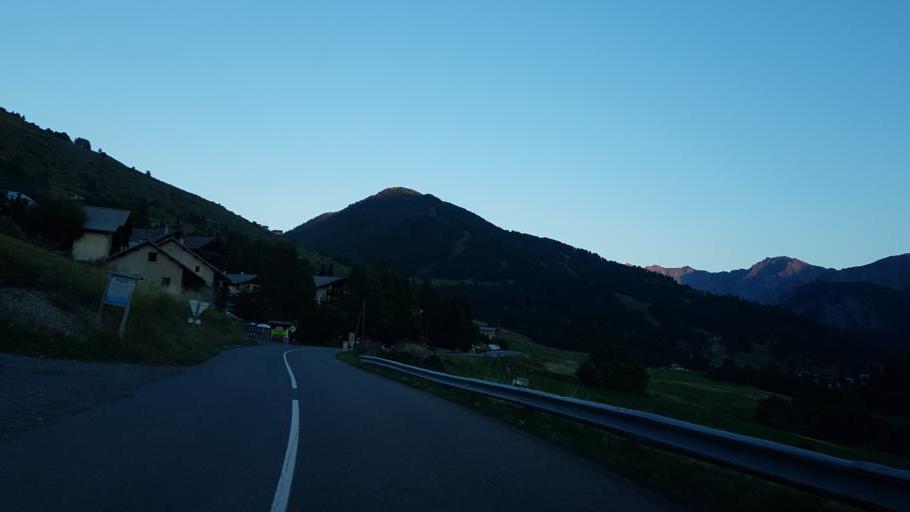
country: FR
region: Provence-Alpes-Cote d'Azur
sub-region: Departement des Hautes-Alpes
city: Guillestre
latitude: 44.7309
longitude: 6.8407
